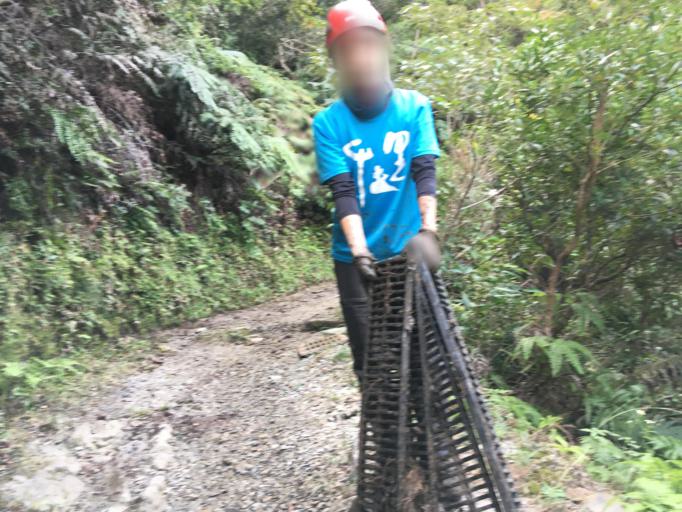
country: TW
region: Taiwan
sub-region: Yilan
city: Yilan
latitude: 24.8459
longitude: 121.7767
